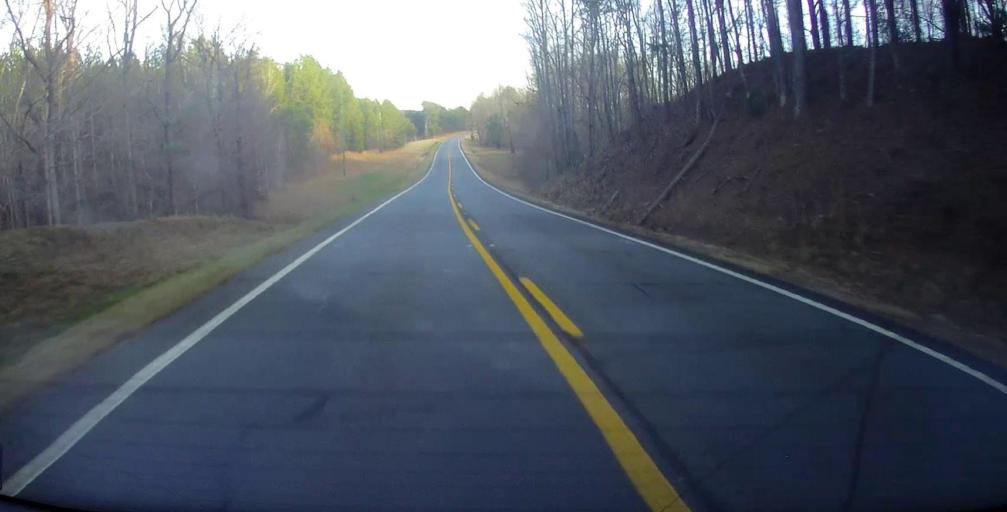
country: US
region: Georgia
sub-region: Talbot County
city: Sardis
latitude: 32.7918
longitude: -84.5391
